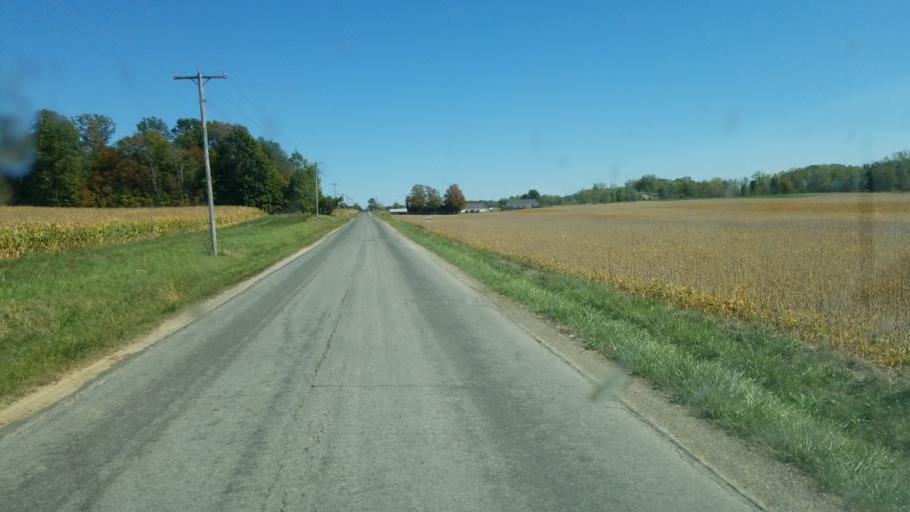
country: US
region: Ohio
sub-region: Huron County
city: Greenwich
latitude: 40.9933
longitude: -82.5197
